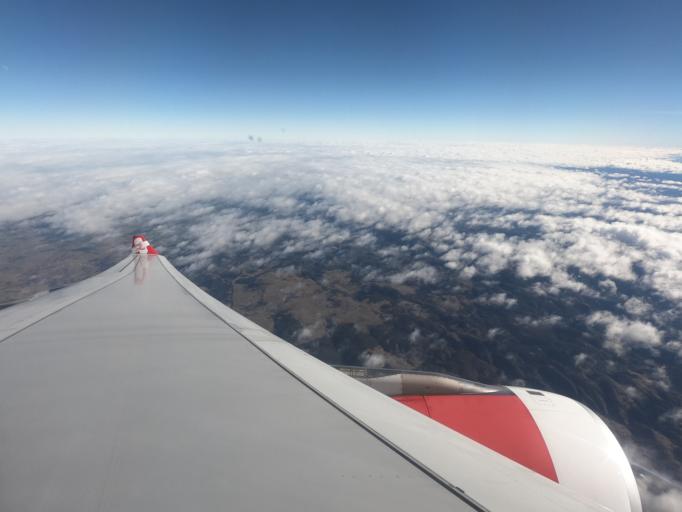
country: AU
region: New South Wales
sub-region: Wingecarribee
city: Bundanoon
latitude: -34.4691
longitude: 150.0044
